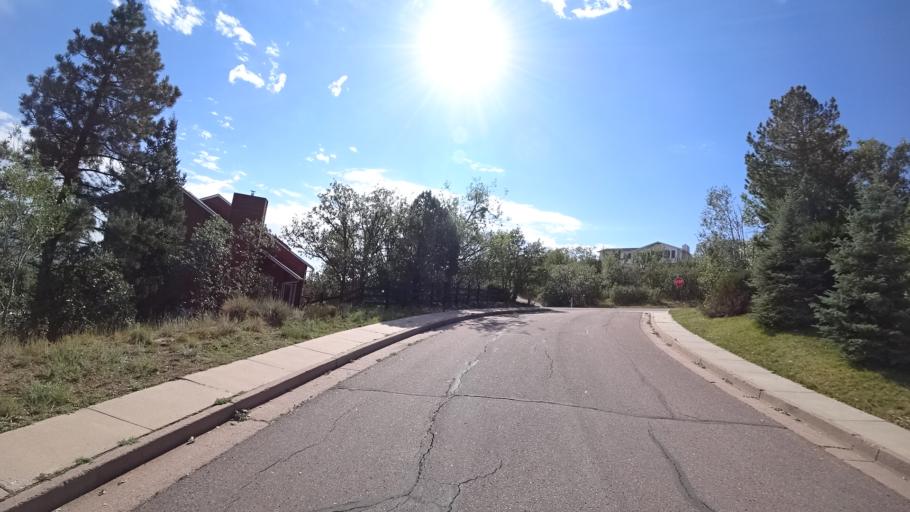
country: US
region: Colorado
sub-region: El Paso County
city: Stratmoor
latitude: 38.7666
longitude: -104.8232
